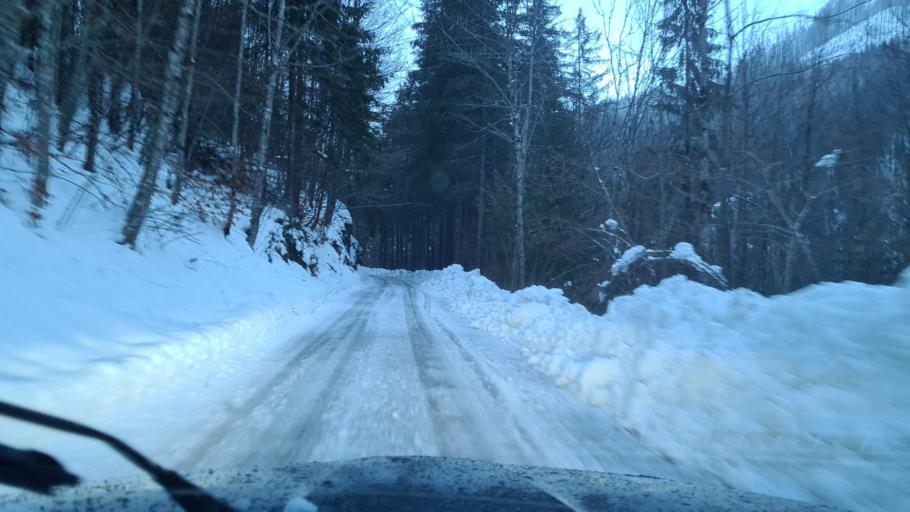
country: AT
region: Salzburg
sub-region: Politischer Bezirk Sankt Johann im Pongau
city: Werfen
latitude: 47.4818
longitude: 13.1541
